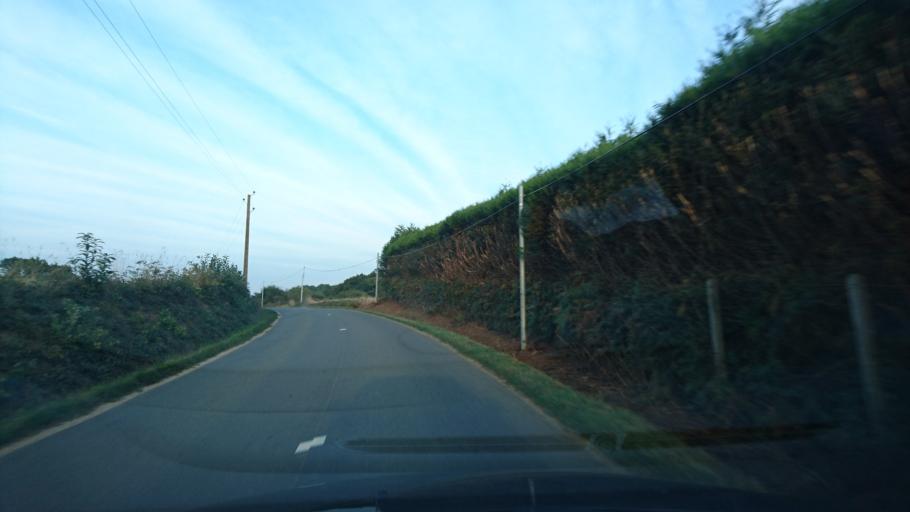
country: FR
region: Brittany
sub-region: Departement d'Ille-et-Vilaine
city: Sixt-sur-Aff
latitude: 47.8093
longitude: -2.0461
